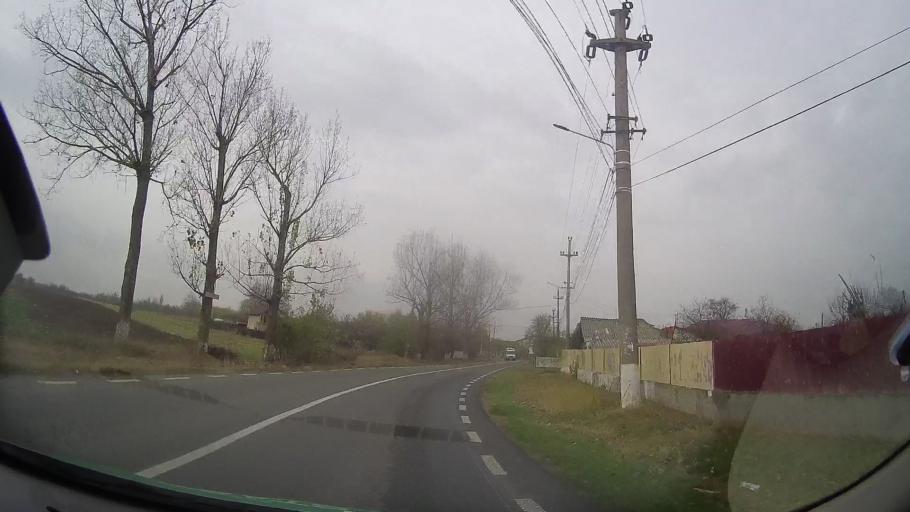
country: RO
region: Ilfov
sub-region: Comuna Gruiu
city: Lipia
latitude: 44.7147
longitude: 26.2527
